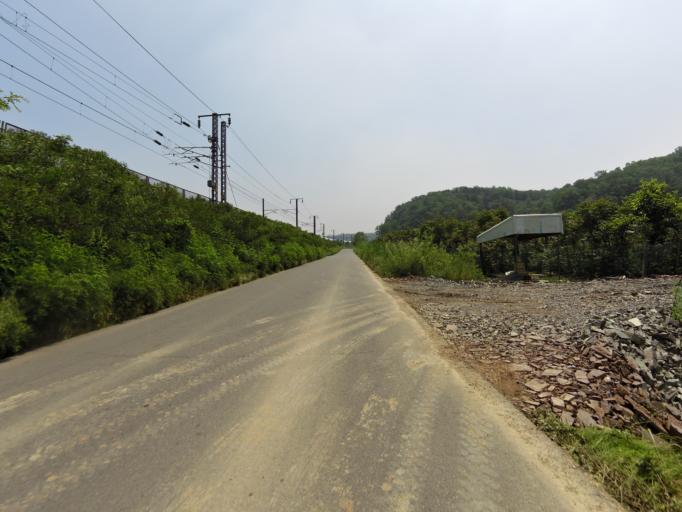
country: KR
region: Gyeongsangbuk-do
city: Gyeongsan-si
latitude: 35.8518
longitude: 128.7027
